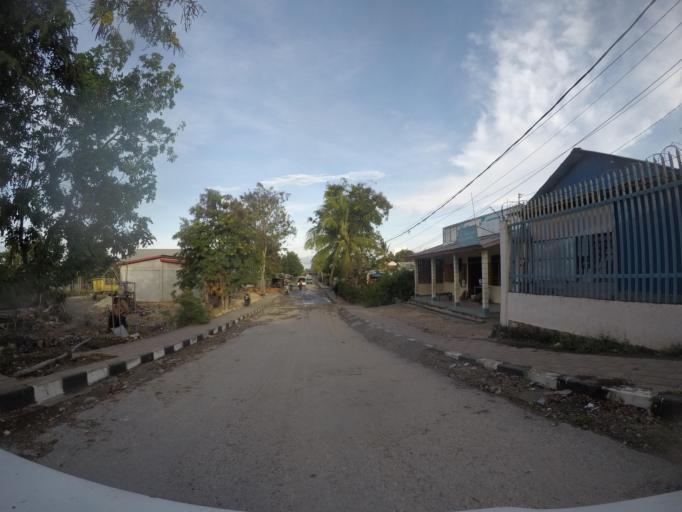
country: TL
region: Baucau
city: Baucau
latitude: -8.4763
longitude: 126.4566
